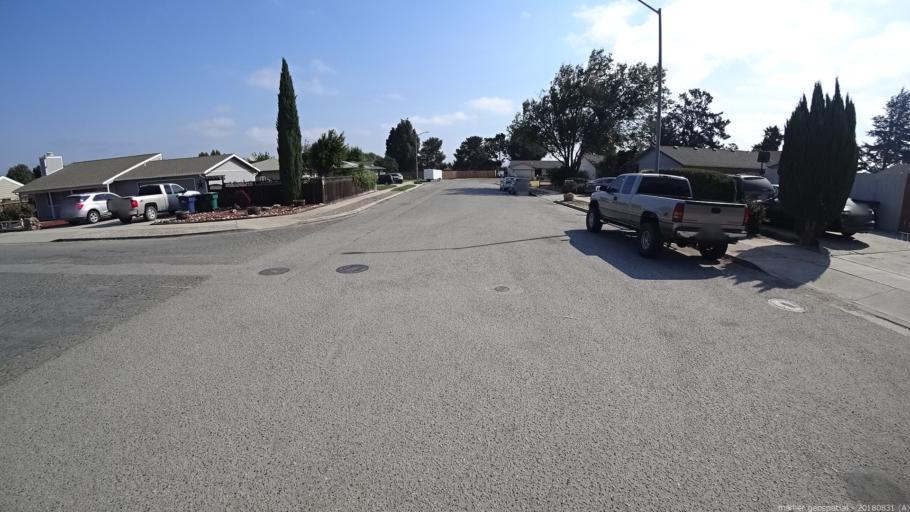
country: US
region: California
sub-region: Monterey County
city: King City
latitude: 36.1867
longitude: -121.1458
